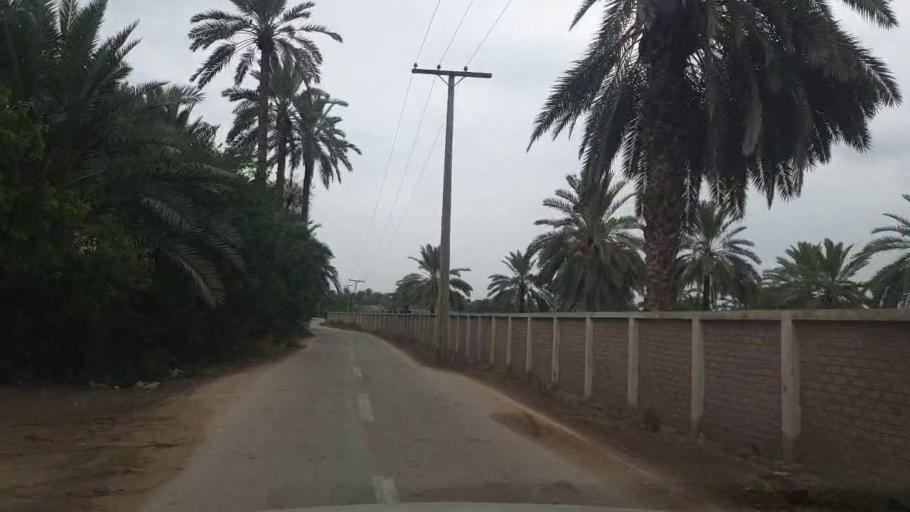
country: PK
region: Sindh
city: Khairpur
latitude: 27.5440
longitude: 68.7548
